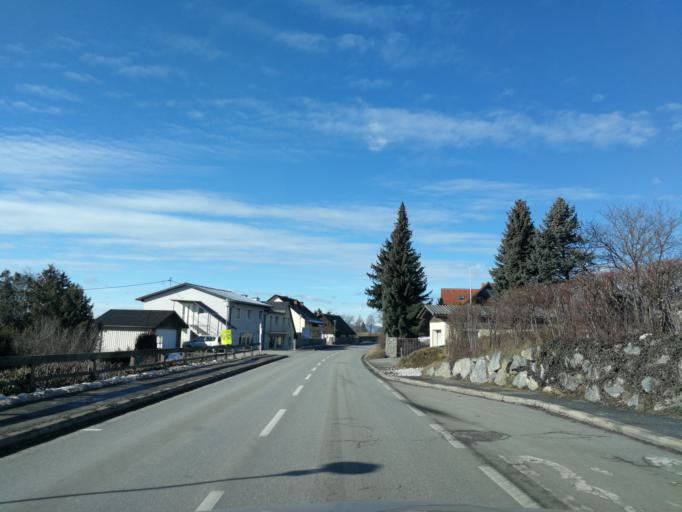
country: AT
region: Styria
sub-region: Politischer Bezirk Graz-Umgebung
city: Nestelbach bei Graz
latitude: 47.0551
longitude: 15.6062
